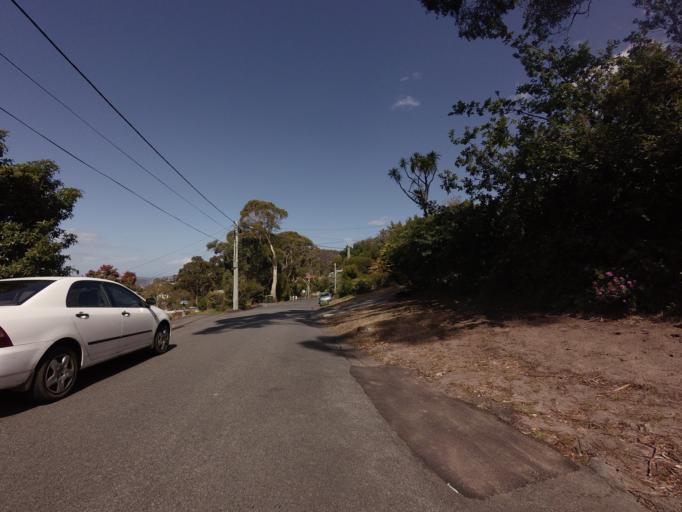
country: AU
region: Tasmania
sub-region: Hobart
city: Dynnyrne
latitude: -42.9124
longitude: 147.3258
